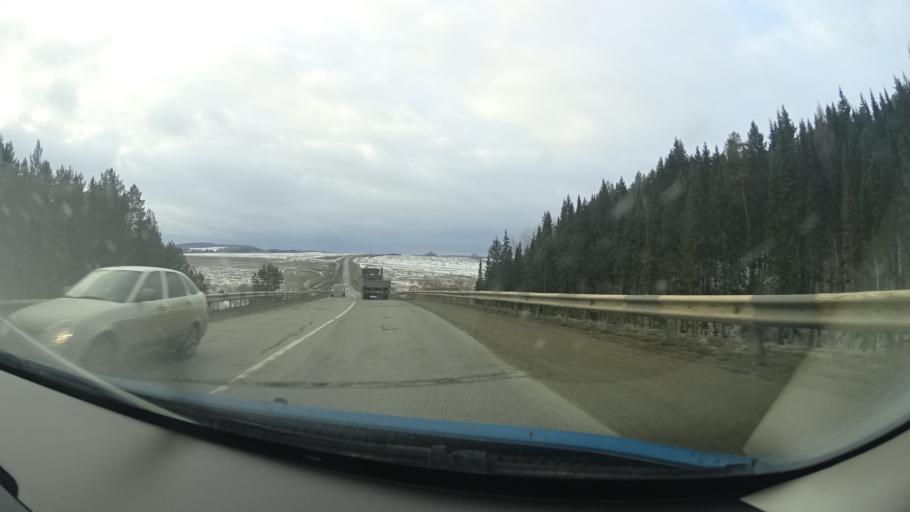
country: RU
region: Perm
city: Osa
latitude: 57.2573
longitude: 55.5762
